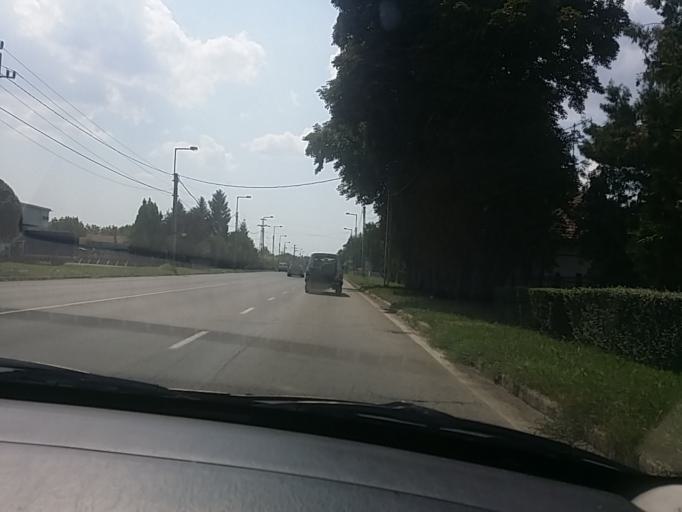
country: HU
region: Tolna
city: Dombovar
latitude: 46.3910
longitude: 18.1445
